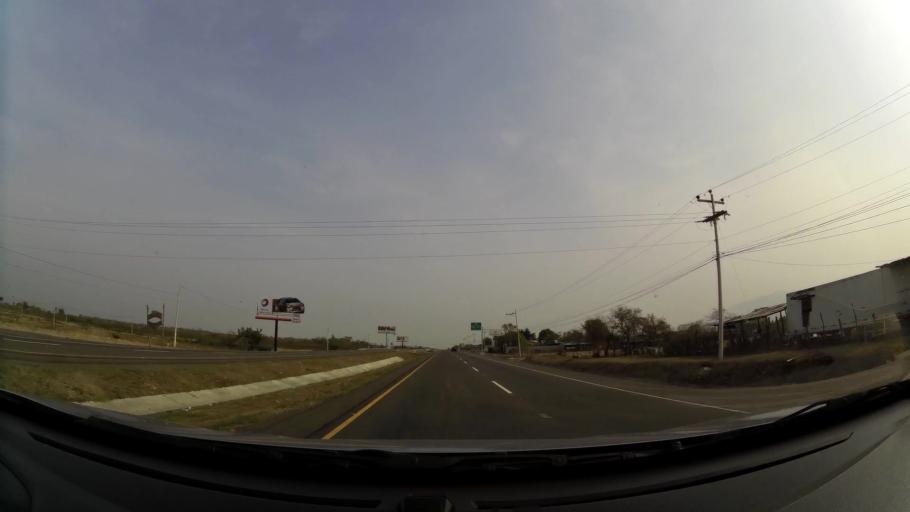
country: HN
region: Comayagua
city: Villa de San Antonio
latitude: 14.3395
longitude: -87.5919
